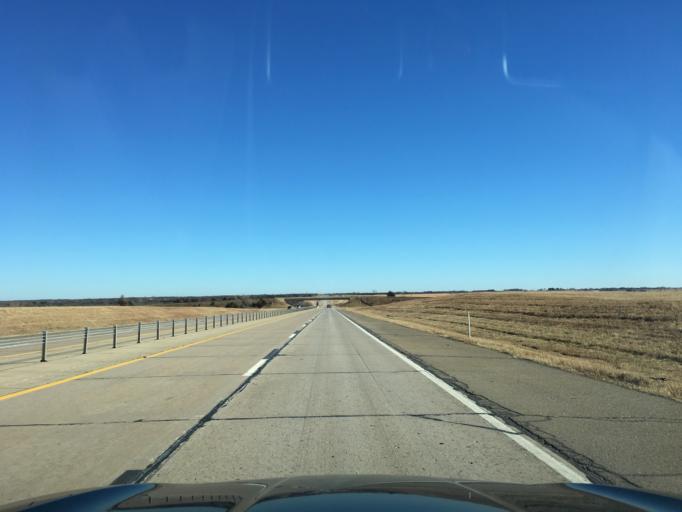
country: US
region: Oklahoma
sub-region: Pawnee County
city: Pawnee
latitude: 36.2252
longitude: -96.8594
